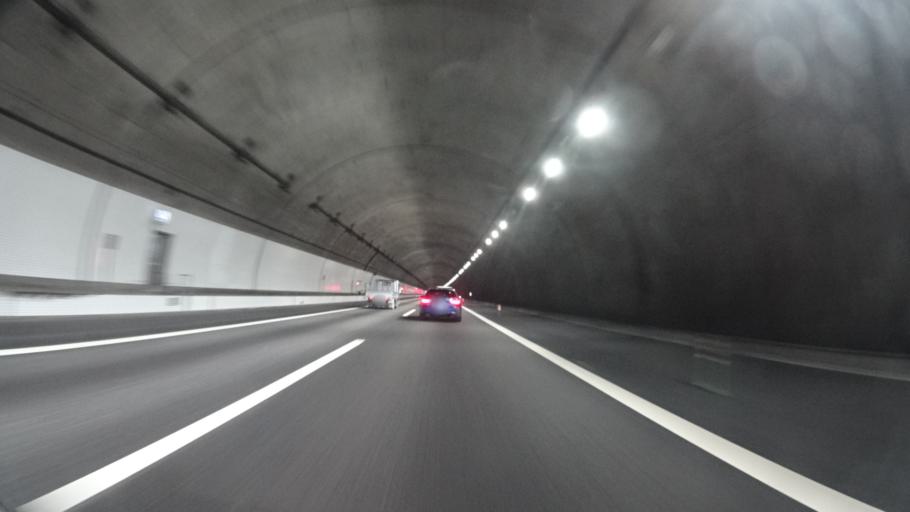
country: JP
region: Shiga Prefecture
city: Minakuchicho-matoba
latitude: 34.9217
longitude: 136.1221
